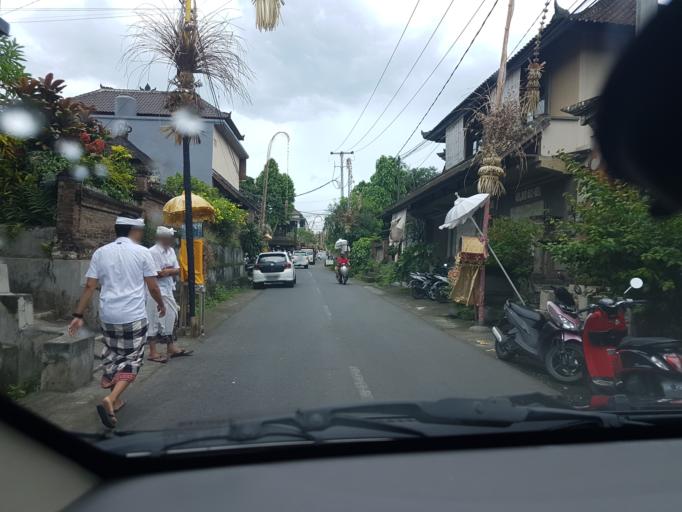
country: ID
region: Bali
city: Banjar Pande
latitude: -8.5043
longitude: 115.2476
